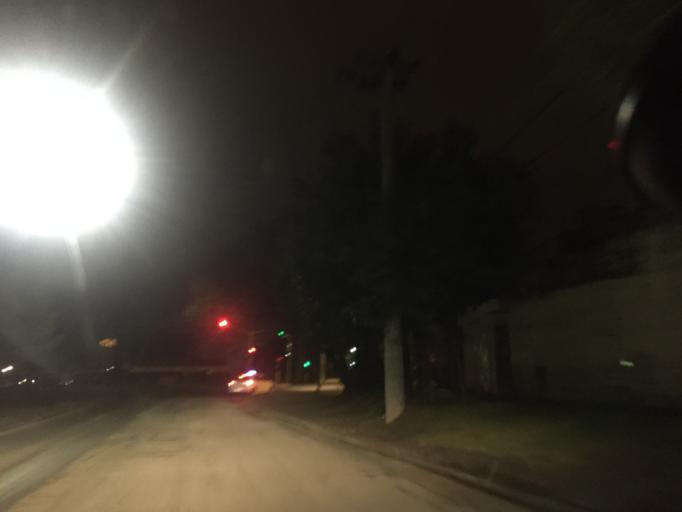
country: AR
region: Cordoba
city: Villa Allende
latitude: -31.3026
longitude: -64.2838
